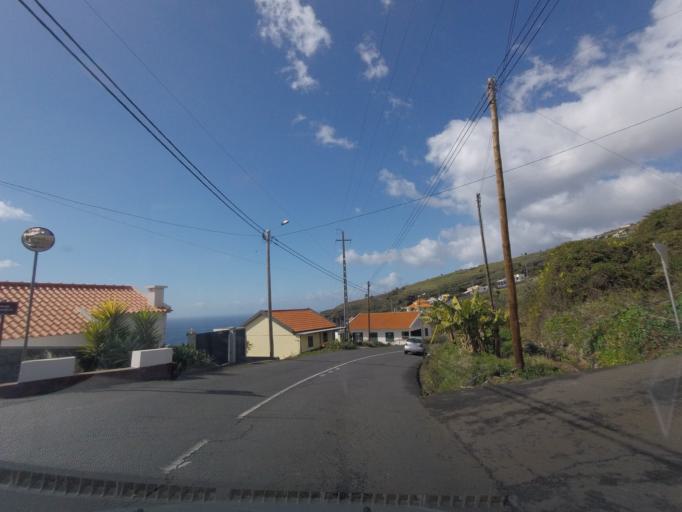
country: PT
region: Madeira
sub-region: Calheta
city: Estreito da Calheta
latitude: 32.7327
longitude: -17.1954
